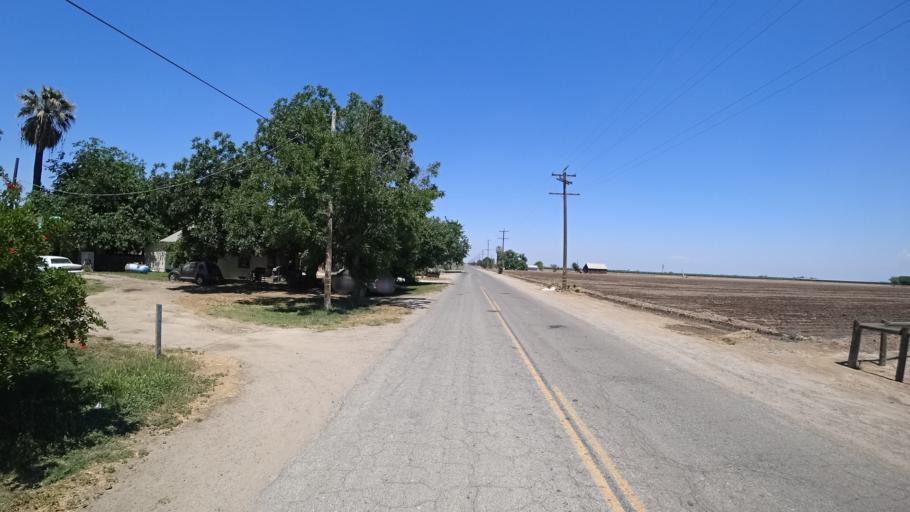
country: US
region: California
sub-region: Kings County
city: Armona
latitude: 36.3580
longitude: -119.7270
